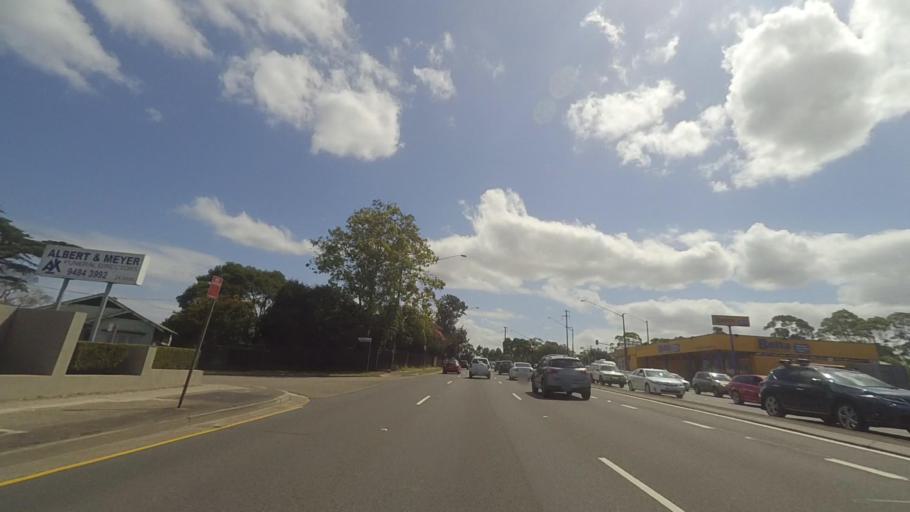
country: AU
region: New South Wales
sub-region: Hornsby Shire
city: Pennant Hills
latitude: -33.7324
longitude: 151.0788
